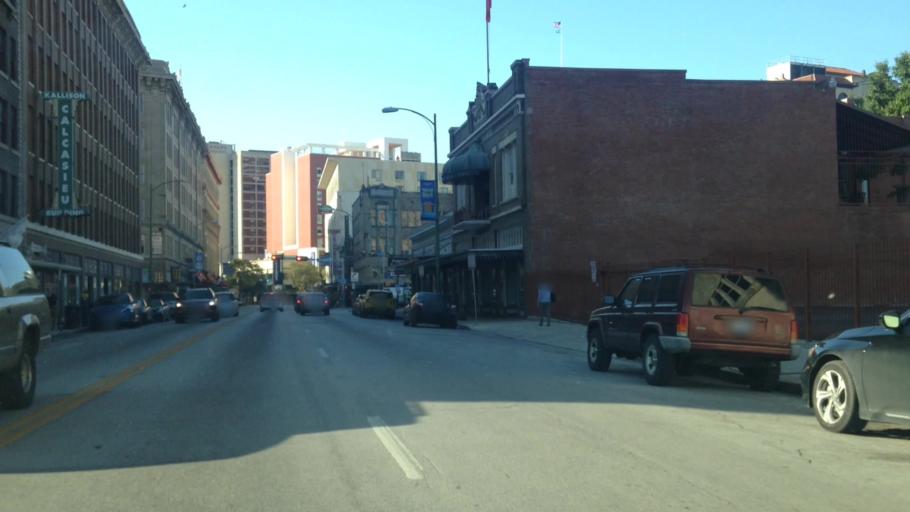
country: US
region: Texas
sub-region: Bexar County
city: San Antonio
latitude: 29.4284
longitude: -98.4873
